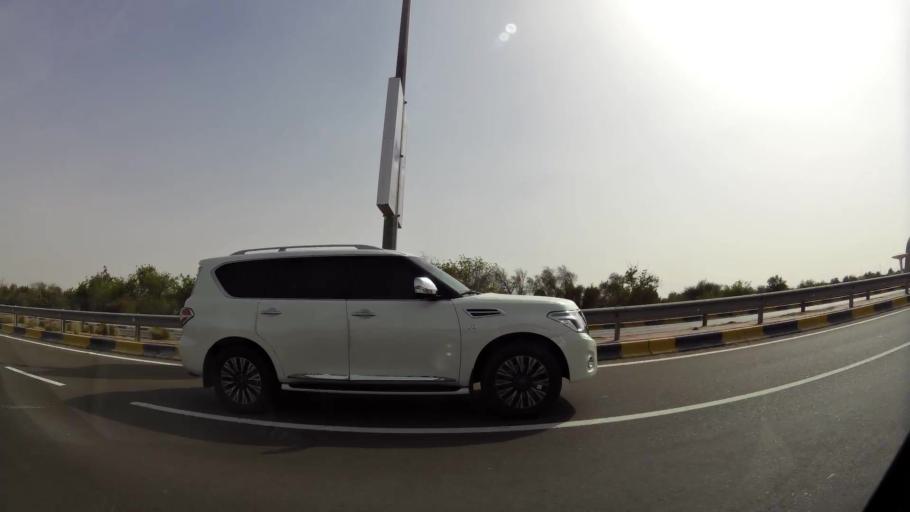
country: AE
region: Abu Dhabi
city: Al Ain
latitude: 24.1797
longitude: 55.6005
